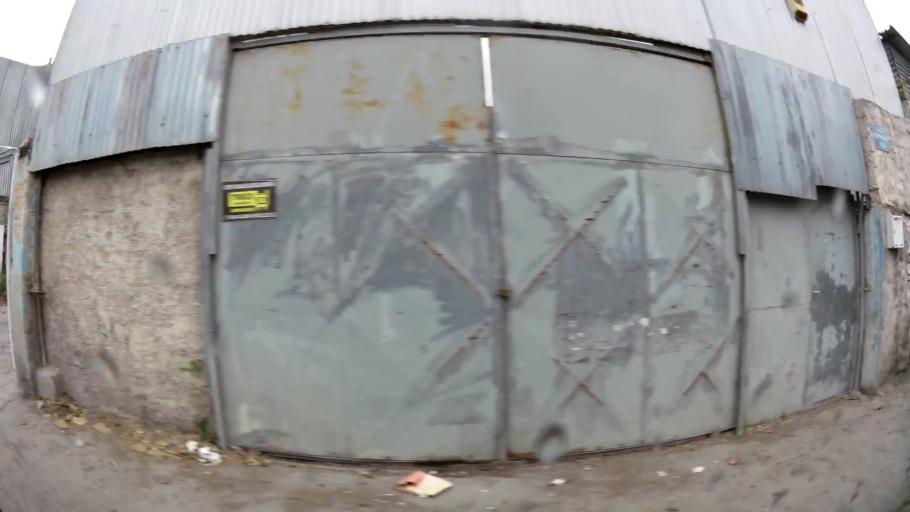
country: GR
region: Attica
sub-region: Nomarchia Athinas
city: Aigaleo
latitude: 37.9805
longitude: 23.6916
